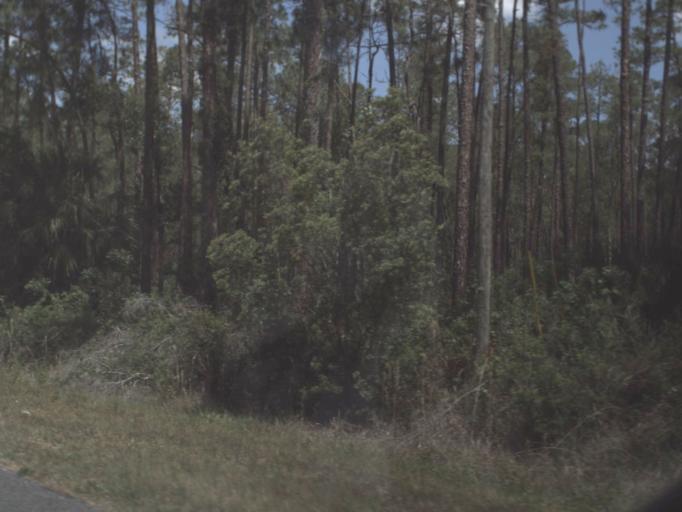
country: US
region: Florida
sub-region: Marion County
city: Silver Springs Shores
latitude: 29.2124
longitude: -81.9528
